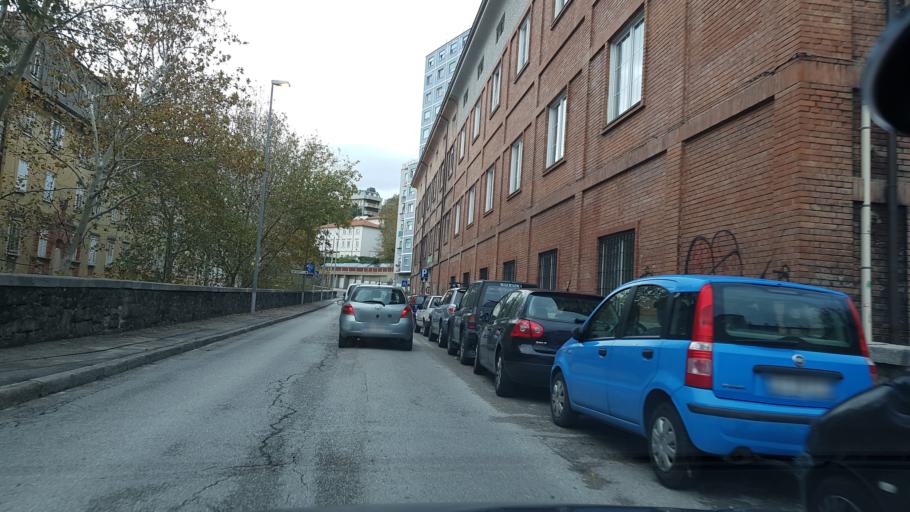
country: IT
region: Friuli Venezia Giulia
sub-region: Provincia di Trieste
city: Trieste
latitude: 45.6642
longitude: 13.7701
